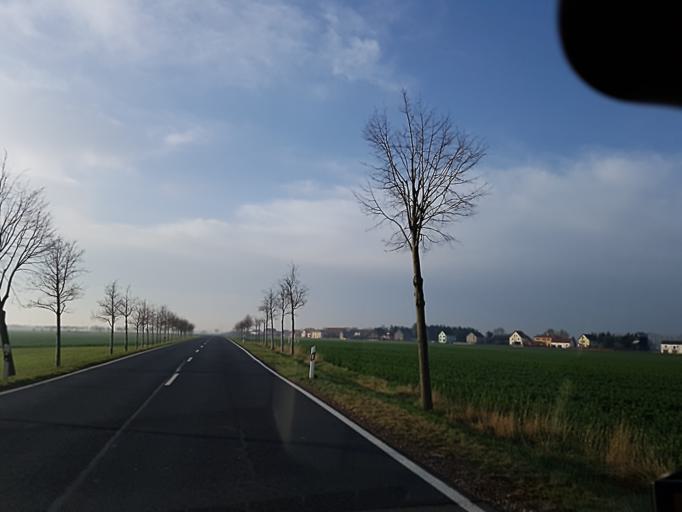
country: DE
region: Saxony
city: Strehla
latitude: 51.3576
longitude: 13.2632
